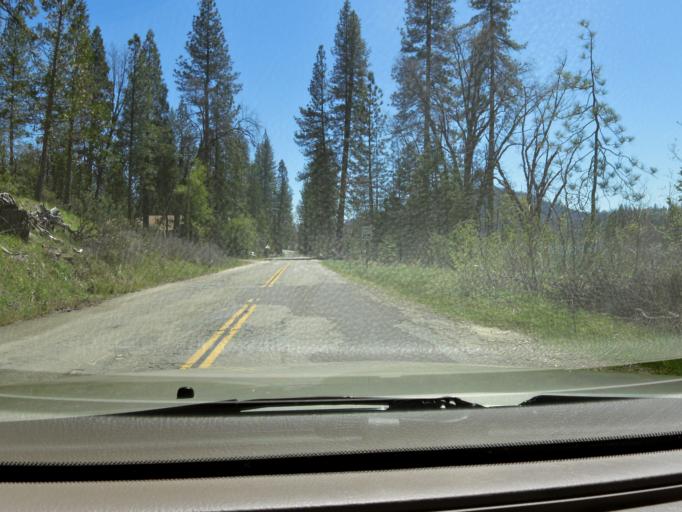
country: US
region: California
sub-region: Madera County
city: Oakhurst
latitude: 37.3329
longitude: -119.5785
